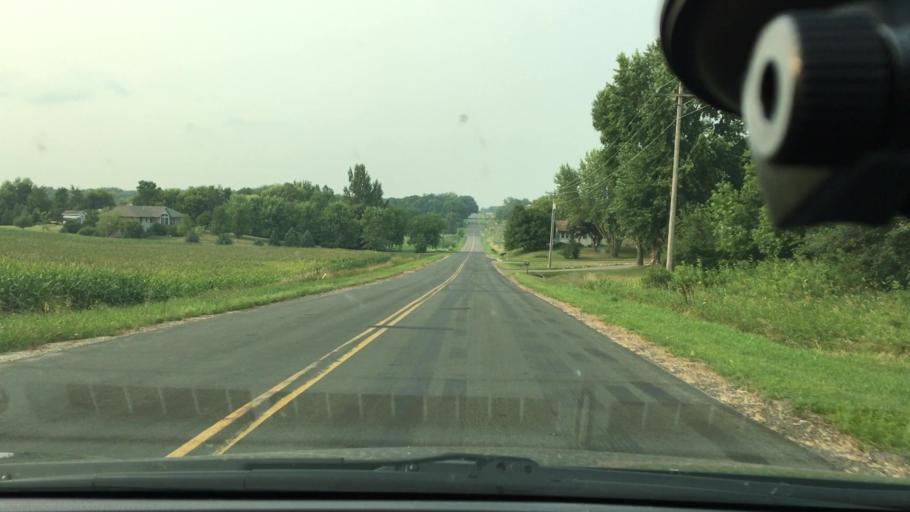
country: US
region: Minnesota
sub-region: Wright County
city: Albertville
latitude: 45.2753
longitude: -93.6841
